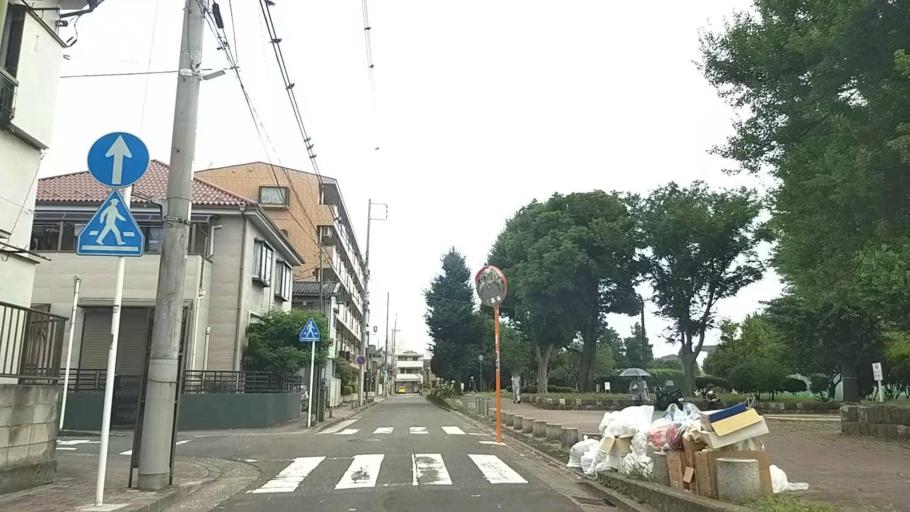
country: JP
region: Kanagawa
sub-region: Kawasaki-shi
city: Kawasaki
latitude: 35.5311
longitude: 139.7294
